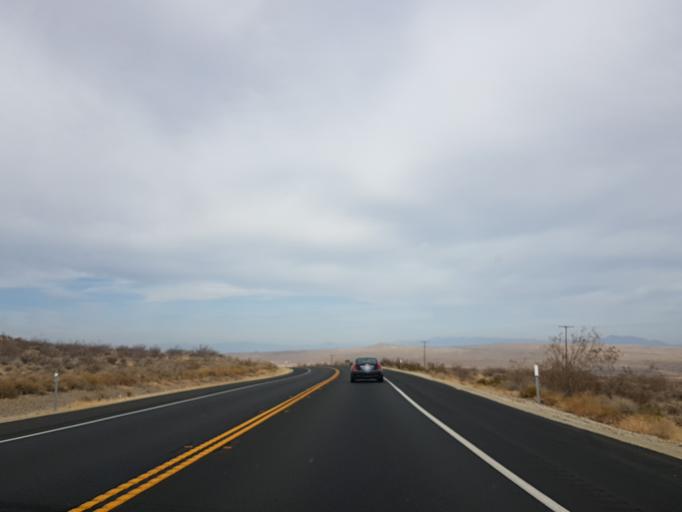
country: US
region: California
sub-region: Kern County
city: Ridgecrest
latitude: 35.4754
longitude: -117.6537
